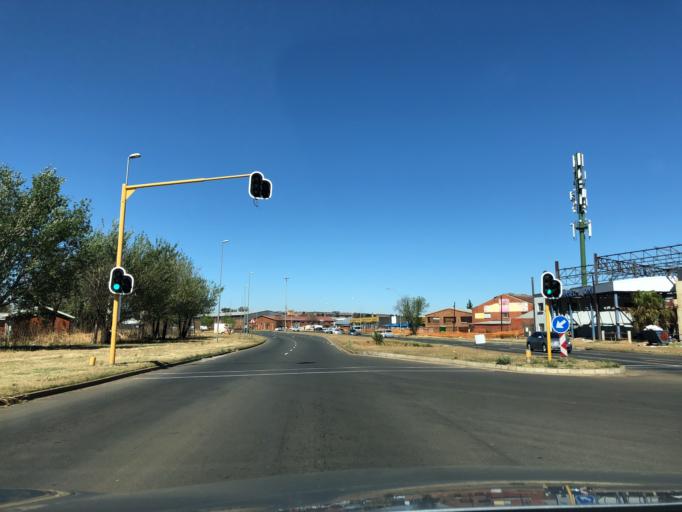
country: ZA
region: KwaZulu-Natal
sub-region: Amajuba District Municipality
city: Newcastle
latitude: -27.7490
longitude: 29.9376
